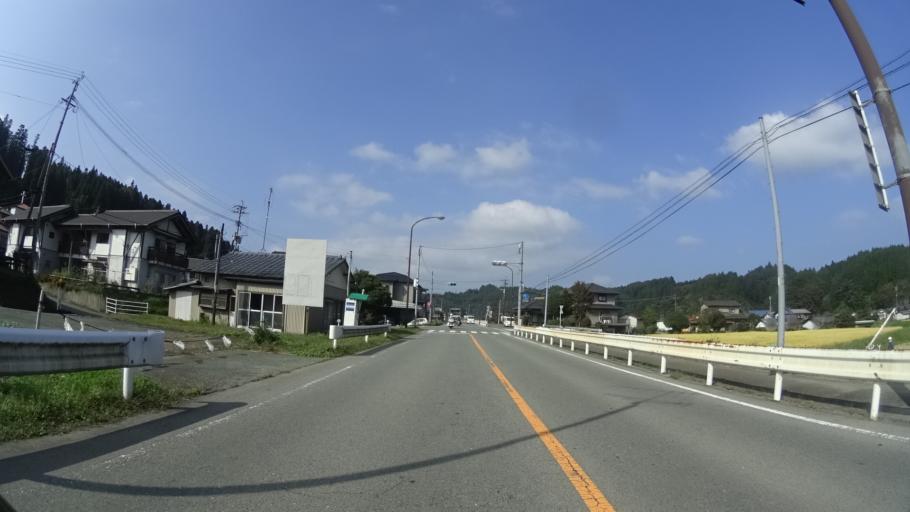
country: JP
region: Kumamoto
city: Aso
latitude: 33.1009
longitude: 131.0679
